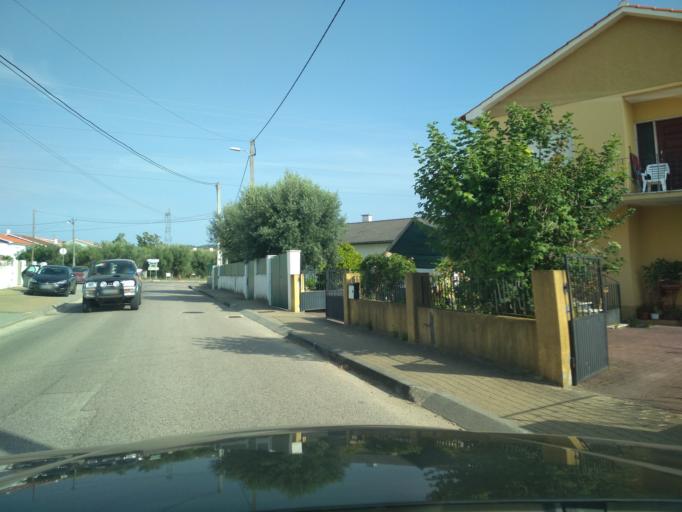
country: PT
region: Coimbra
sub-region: Condeixa-A-Nova
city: Condeixa-a-Nova
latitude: 40.1332
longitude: -8.4669
